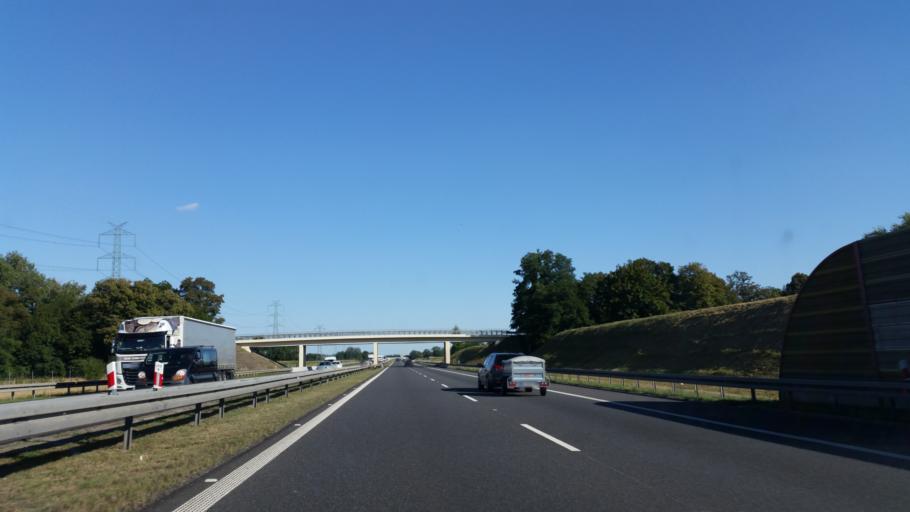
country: PL
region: Lower Silesian Voivodeship
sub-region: Powiat olawski
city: Wierzbno
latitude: 50.9285
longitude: 17.1222
